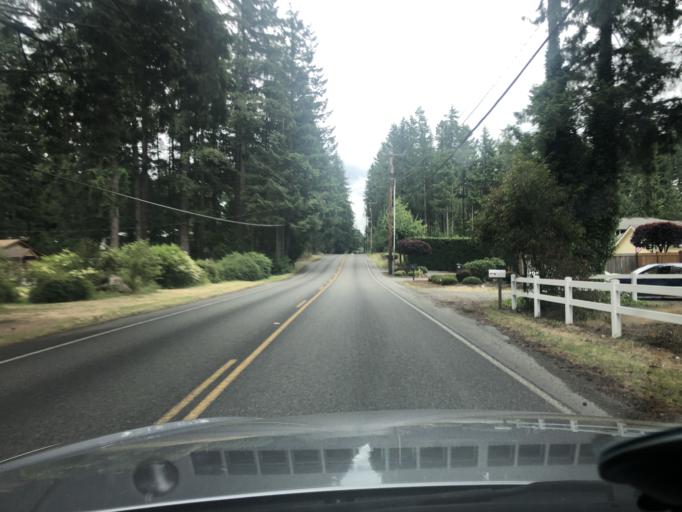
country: US
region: Washington
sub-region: King County
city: Black Diamond
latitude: 47.3335
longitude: -122.0452
